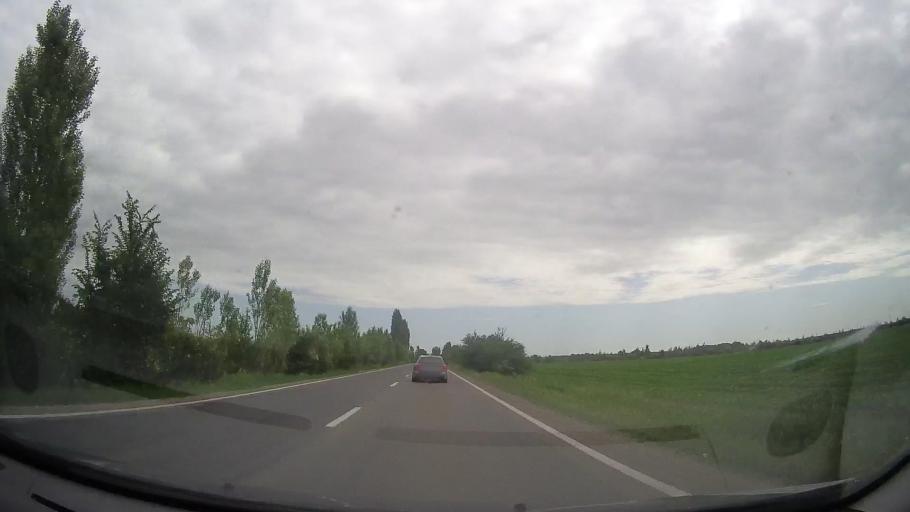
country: RO
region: Prahova
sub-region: Comuna Barcanesti
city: Barcanesti
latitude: 44.8948
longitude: 26.0537
